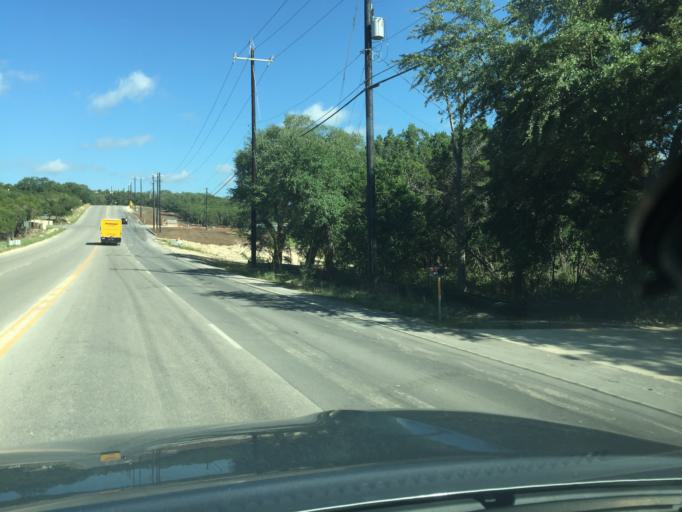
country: US
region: Texas
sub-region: Bexar County
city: Timberwood Park
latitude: 29.7134
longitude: -98.4679
